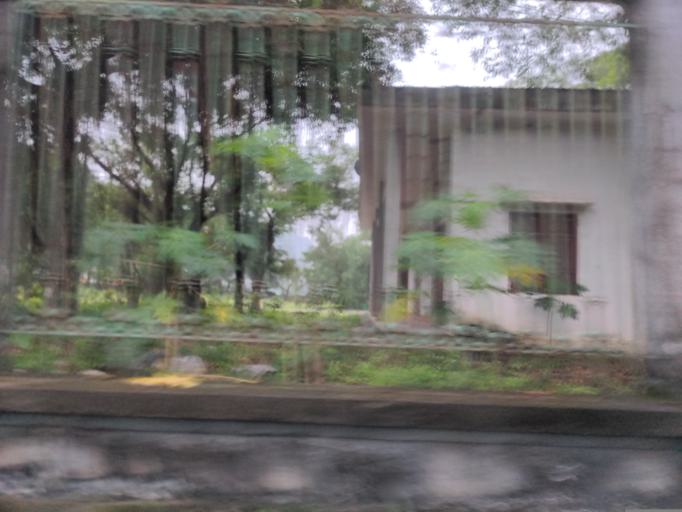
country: VN
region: Ninh Binh
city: Thi Tran Tam Diep
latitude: 20.2094
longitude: 105.9070
